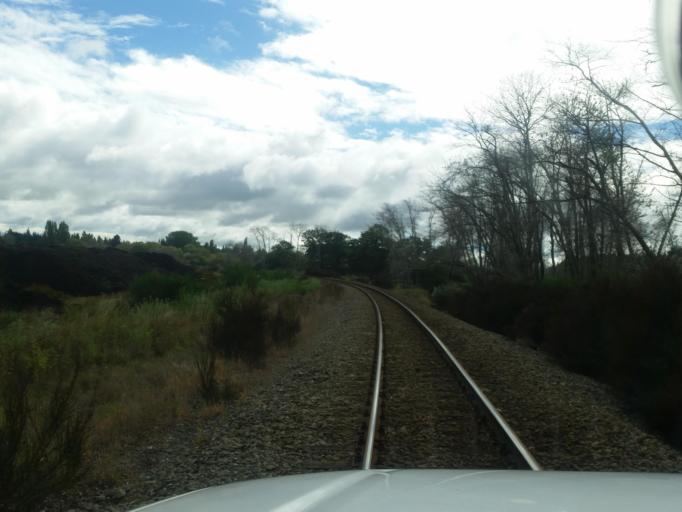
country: NZ
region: Canterbury
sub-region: Waimakariri District
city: Kaiapoi
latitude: -43.4235
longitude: 172.6574
